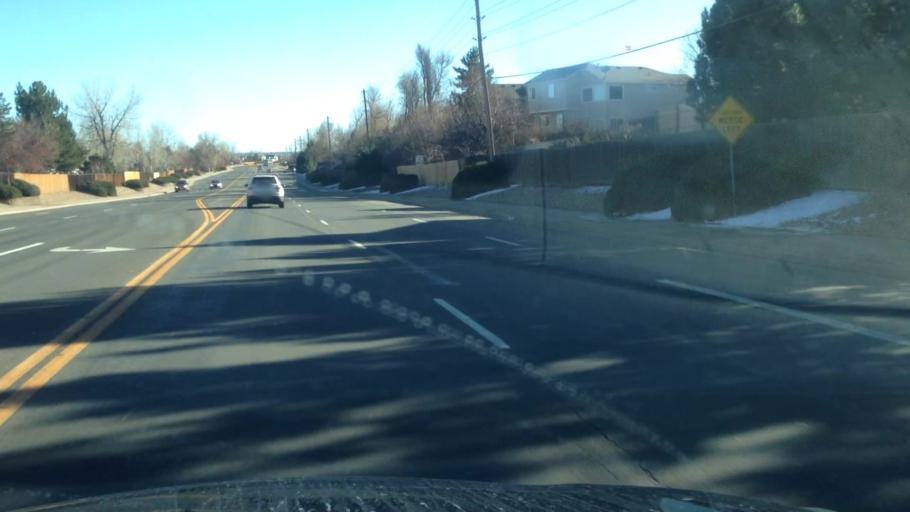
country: US
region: Colorado
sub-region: Arapahoe County
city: Dove Valley
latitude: 39.5647
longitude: -104.8004
